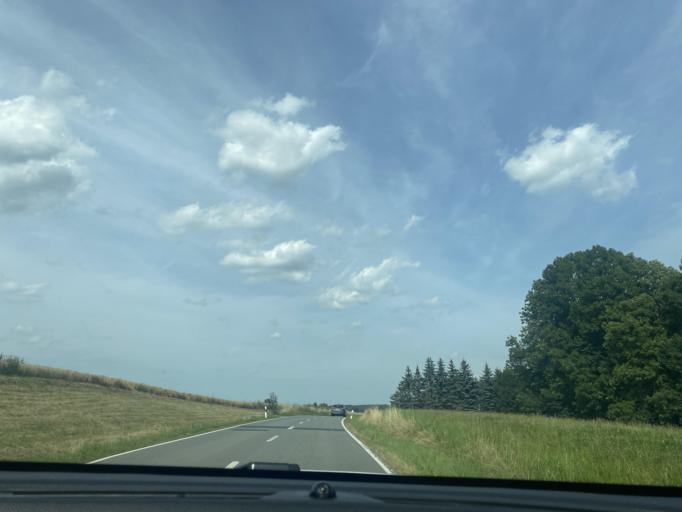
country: DE
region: Saxony
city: Grosshennersdorf
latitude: 50.9858
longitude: 14.7856
